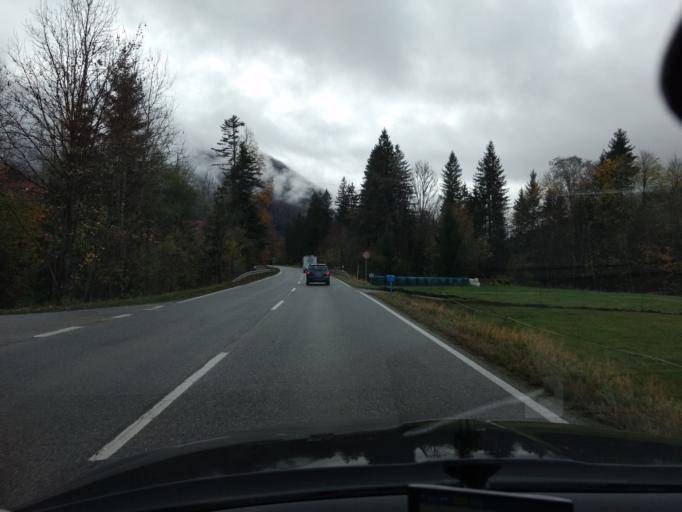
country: DE
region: Bavaria
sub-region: Upper Bavaria
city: Lenggries
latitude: 47.6315
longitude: 11.5942
